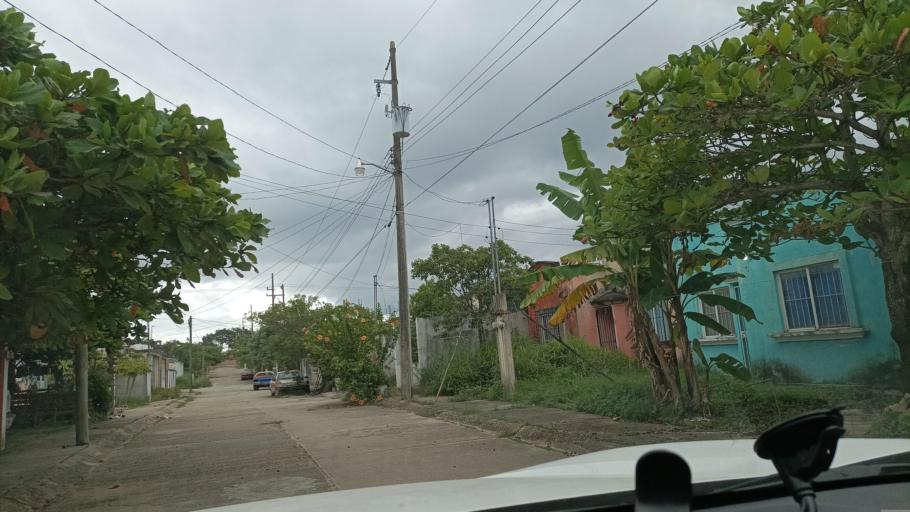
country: MX
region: Veracruz
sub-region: Soconusco
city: Fraccionamiento Santa Cruz
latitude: 17.9708
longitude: -94.8947
